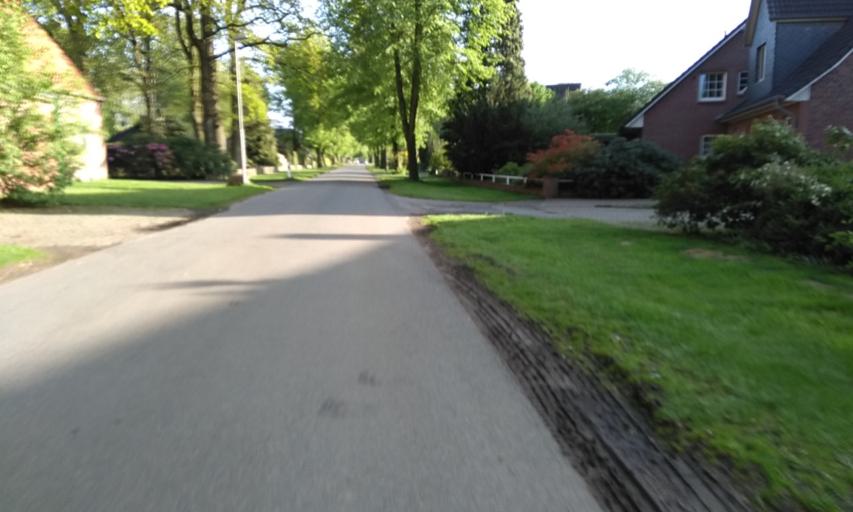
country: DE
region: Lower Saxony
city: Harsefeld
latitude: 53.4185
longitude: 9.5511
